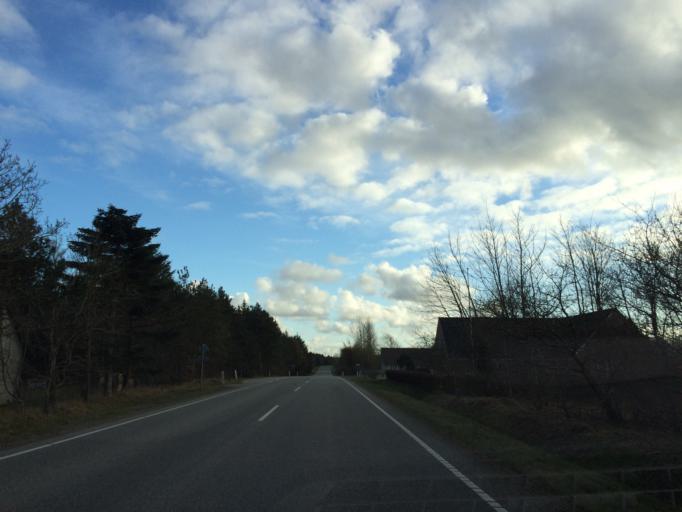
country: DK
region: Central Jutland
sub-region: Holstebro Kommune
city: Ulfborg
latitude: 56.3708
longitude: 8.3326
